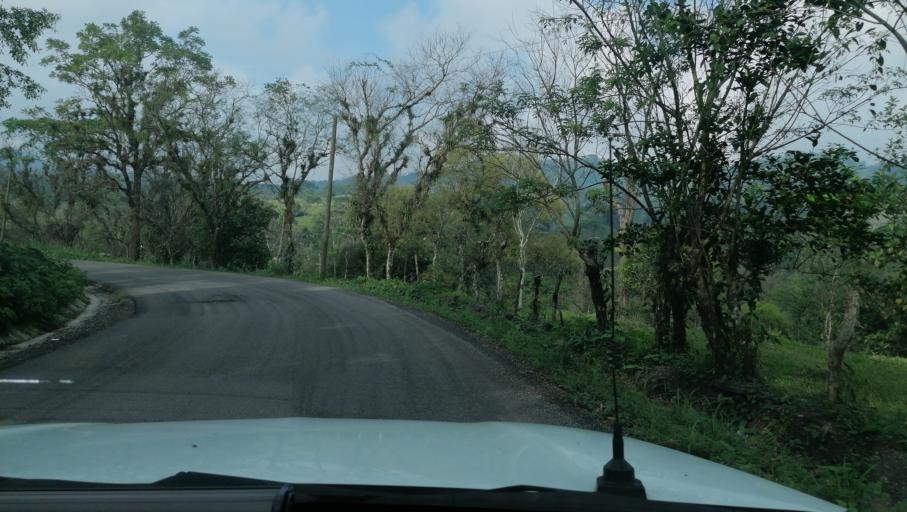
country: MX
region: Chiapas
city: Pichucalco
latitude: 17.5340
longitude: -93.1546
